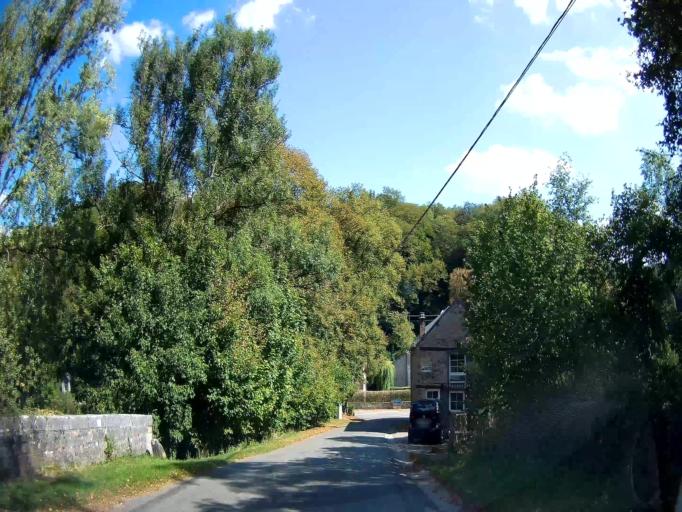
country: BE
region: Wallonia
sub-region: Province de Namur
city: Houyet
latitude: 50.2219
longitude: 4.9857
